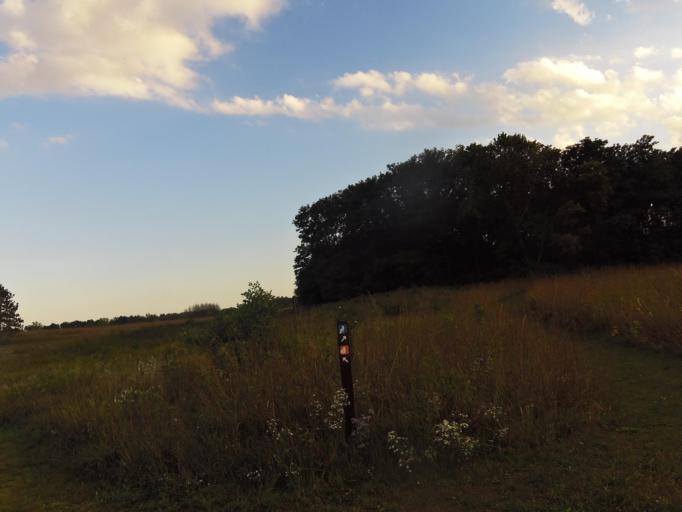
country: US
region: Minnesota
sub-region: Washington County
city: Lake Saint Croix Beach
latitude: 44.9349
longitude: -92.7920
